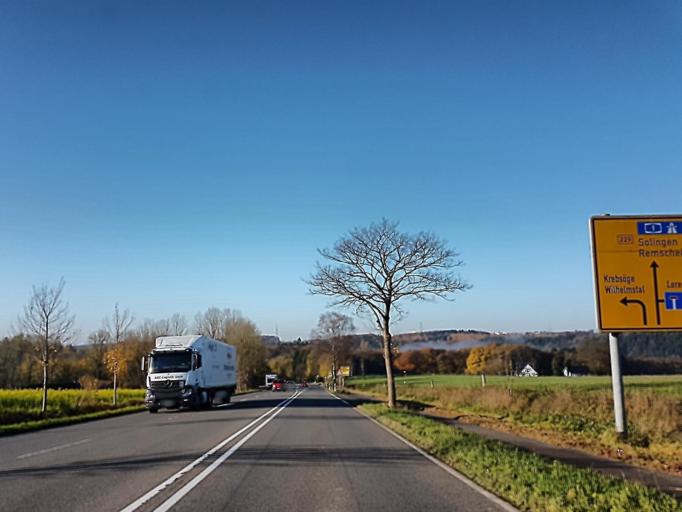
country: DE
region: North Rhine-Westphalia
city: Radevormwald
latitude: 51.2007
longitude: 7.3139
